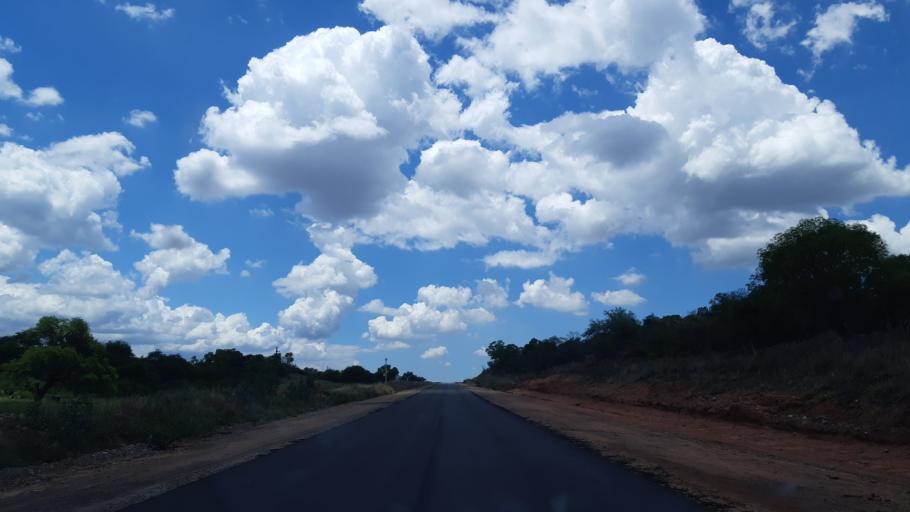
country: AR
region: Jujuy
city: La Mendieta
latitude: -24.4048
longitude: -64.9928
